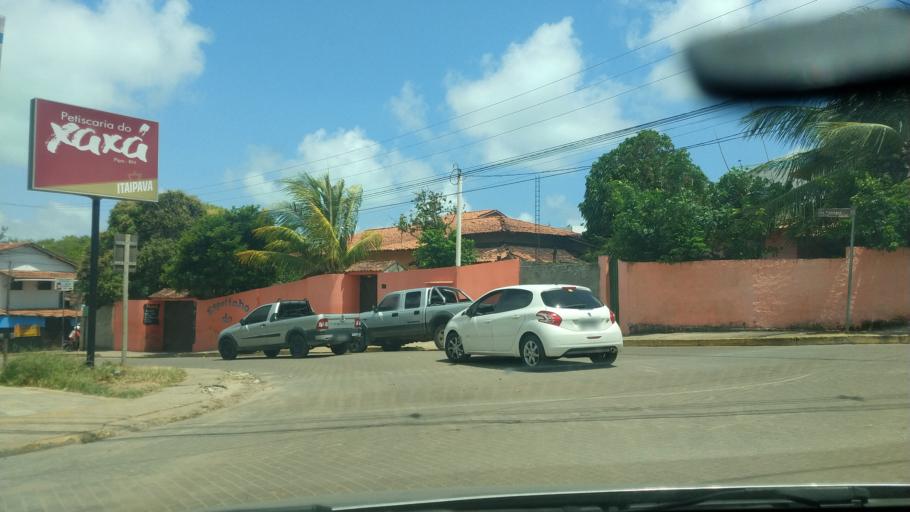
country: BR
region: Rio Grande do Norte
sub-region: Ares
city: Ares
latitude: -6.2334
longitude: -35.0501
